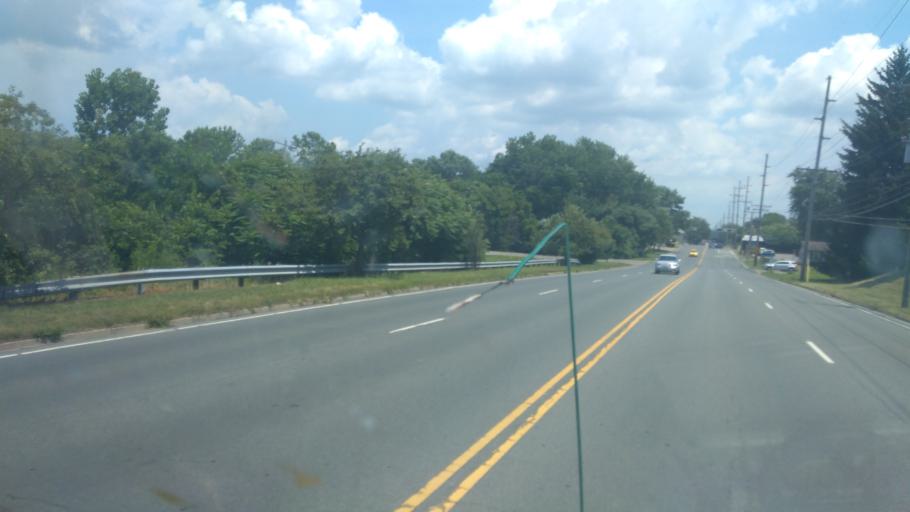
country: US
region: Ohio
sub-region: Fairfield County
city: Lancaster
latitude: 39.7252
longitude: -82.6310
